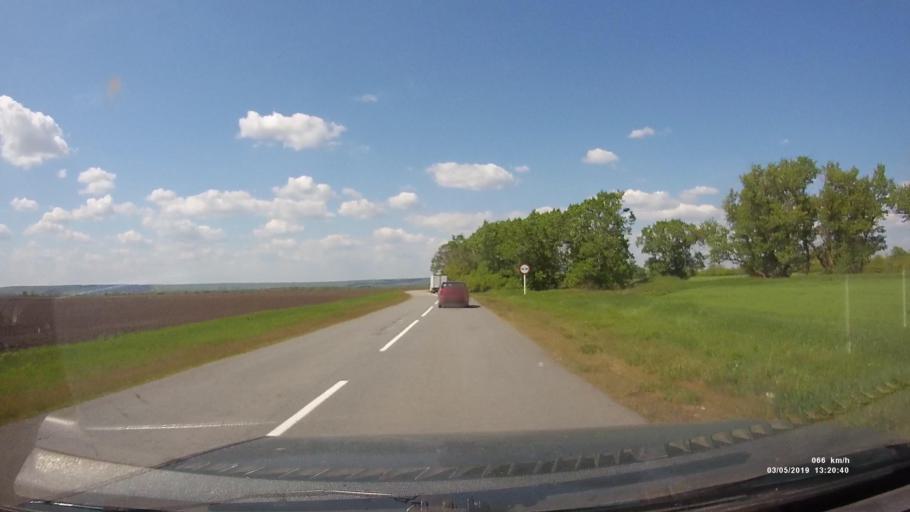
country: RU
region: Rostov
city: Semikarakorsk
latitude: 47.5482
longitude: 40.7518
